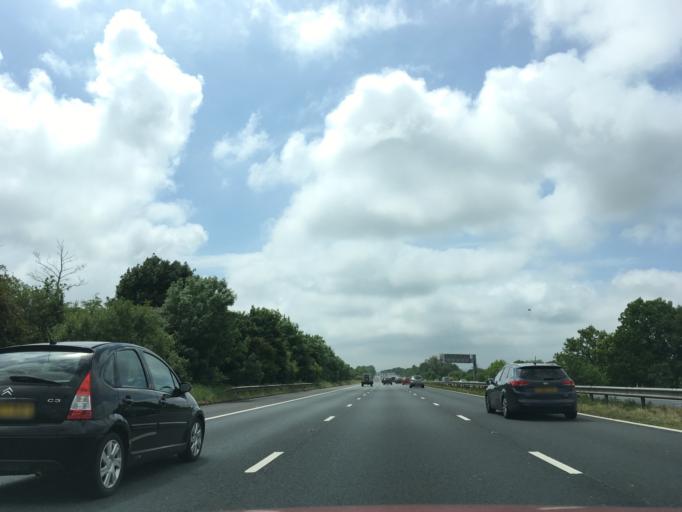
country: GB
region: England
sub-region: Devon
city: Uffculme
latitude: 50.9053
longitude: -3.3678
